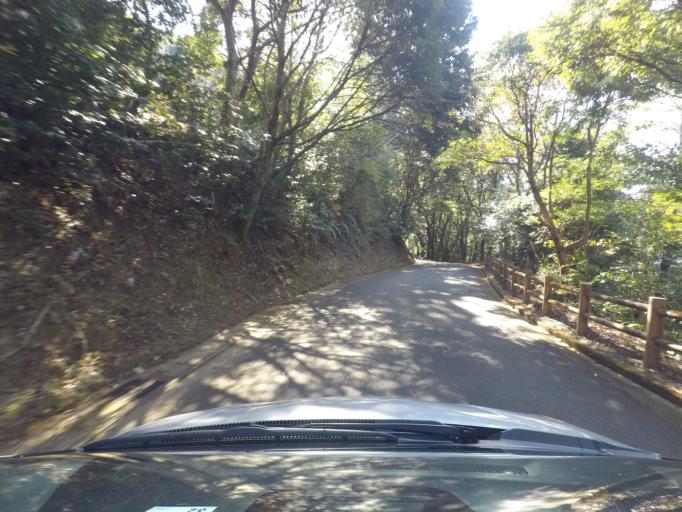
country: JP
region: Miyazaki
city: Kobayashi
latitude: 32.0274
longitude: 131.1937
